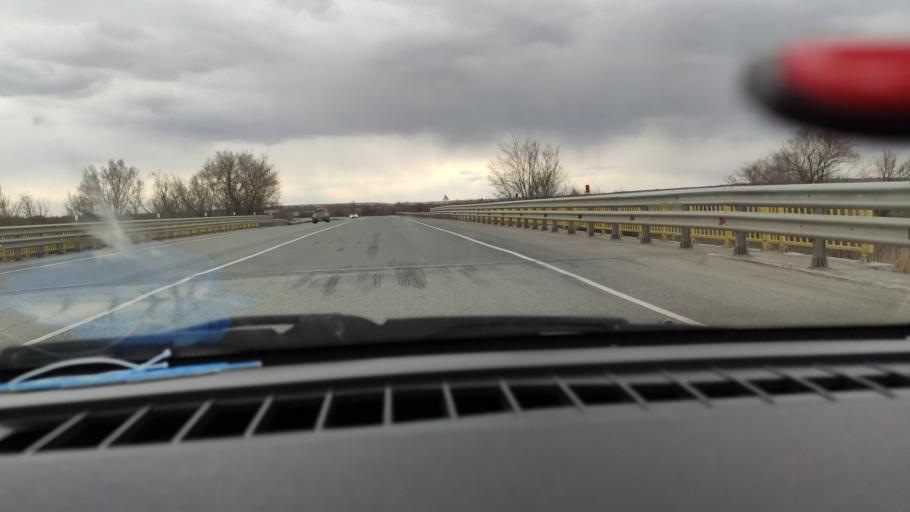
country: RU
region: Saratov
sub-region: Saratovskiy Rayon
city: Saratov
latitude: 51.7205
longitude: 46.0265
